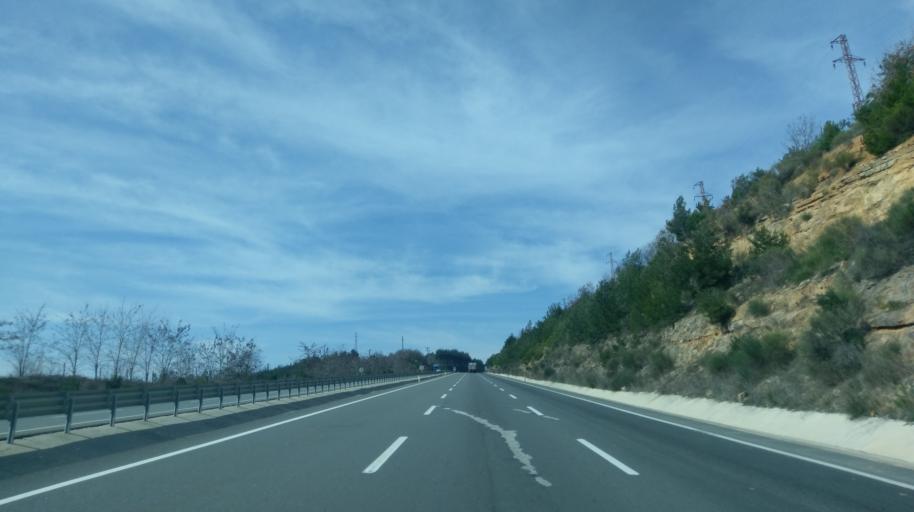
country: TR
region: Canakkale
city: Evrese
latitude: 40.7080
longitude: 26.7765
